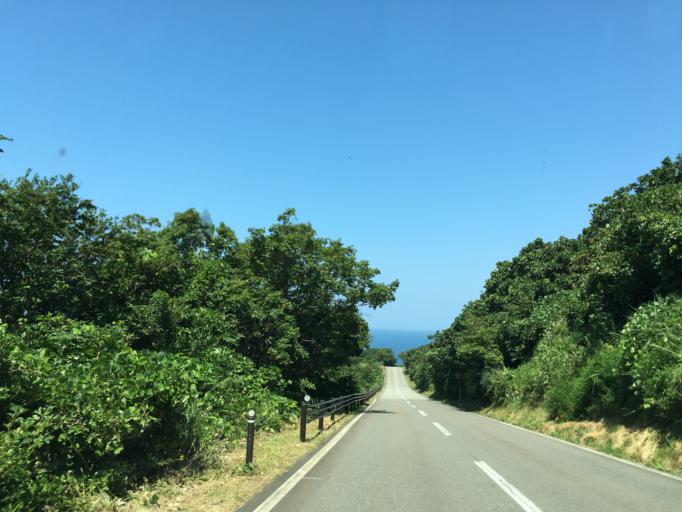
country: JP
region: Akita
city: Tenno
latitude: 39.9339
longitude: 139.7089
